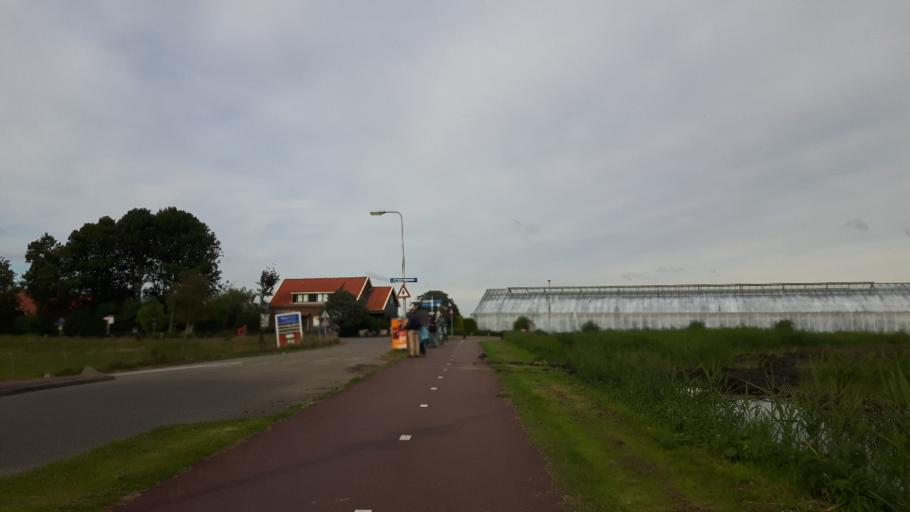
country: NL
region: Utrecht
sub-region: Gemeente De Ronde Venen
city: Mijdrecht
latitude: 52.1689
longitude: 4.8289
